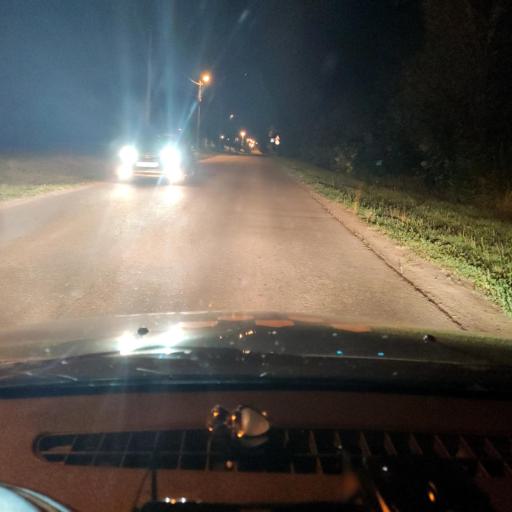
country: RU
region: Belgorod
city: Mayskiy
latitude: 50.5137
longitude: 36.4677
